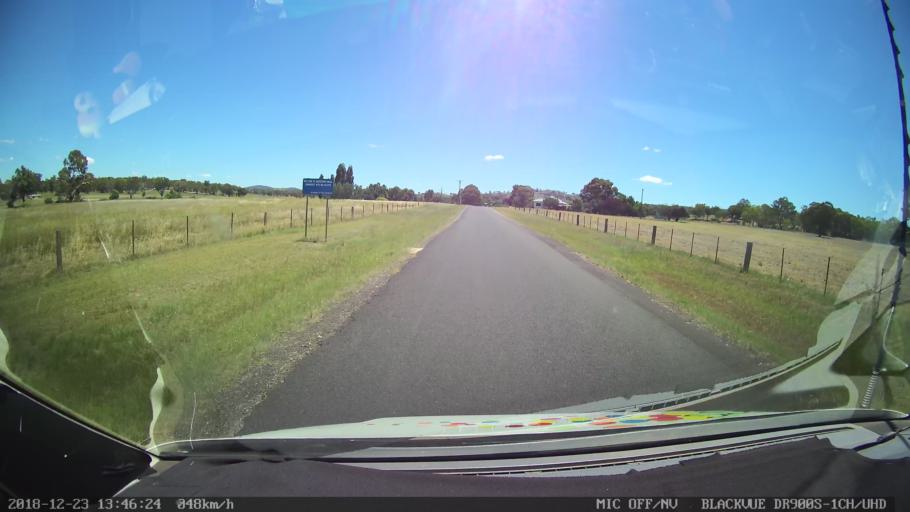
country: AU
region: New South Wales
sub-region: Tamworth Municipality
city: Manilla
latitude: -30.5050
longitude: 151.1194
